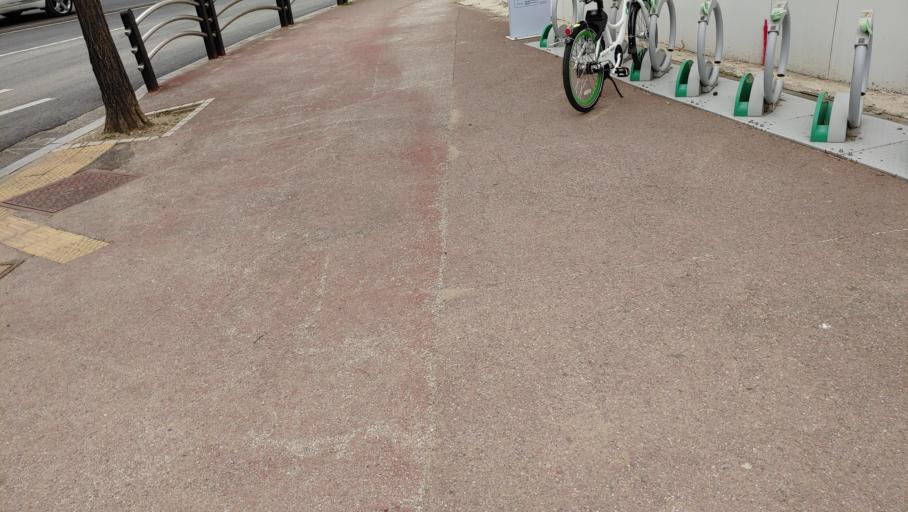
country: KR
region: Gyeonggi-do
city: Seongnam-si
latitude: 37.4888
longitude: 127.0745
